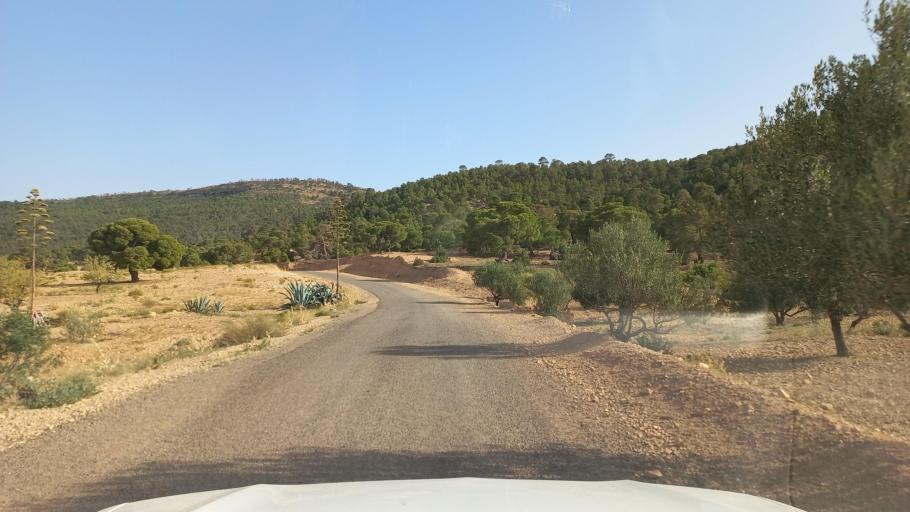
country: TN
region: Al Qasrayn
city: Kasserine
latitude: 35.3347
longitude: 8.8403
